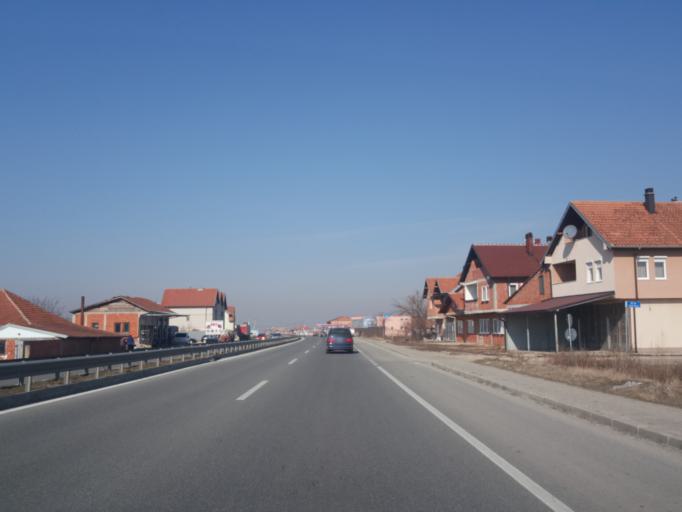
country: XK
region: Pristina
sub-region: Komuna e Obiliqit
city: Obiliq
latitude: 42.7449
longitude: 21.0480
